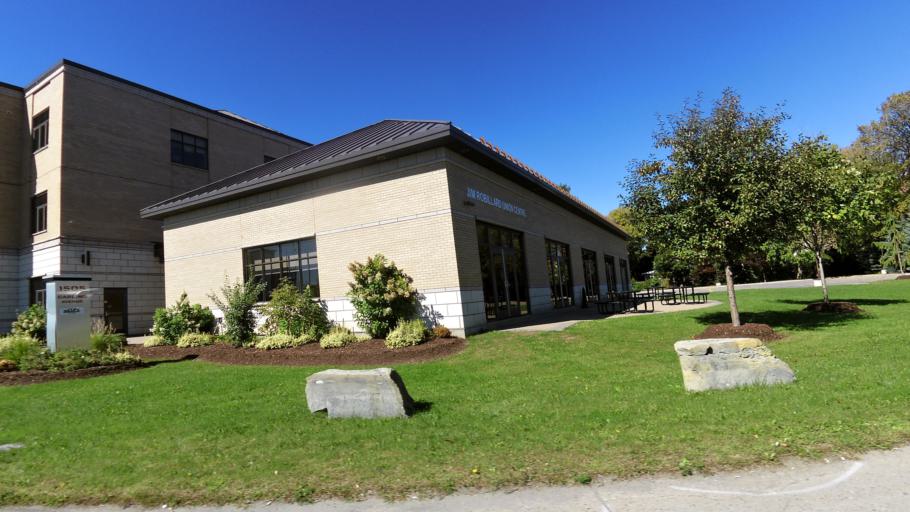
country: CA
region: Ontario
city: Ottawa
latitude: 45.3826
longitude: -75.7425
